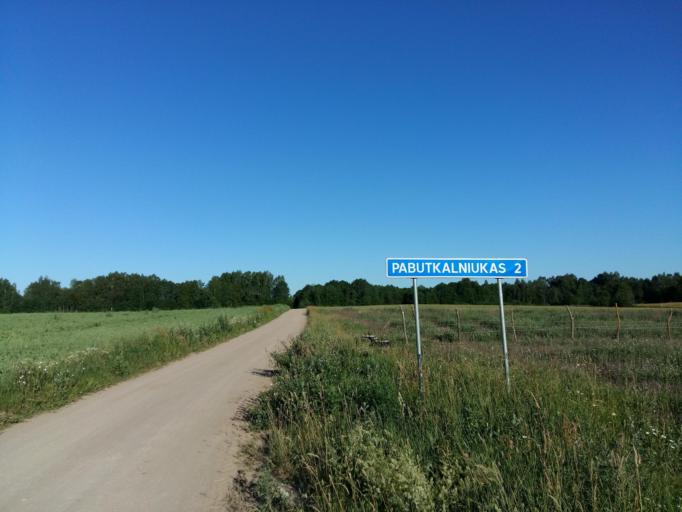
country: LT
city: Kelme
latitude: 55.7261
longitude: 22.6636
